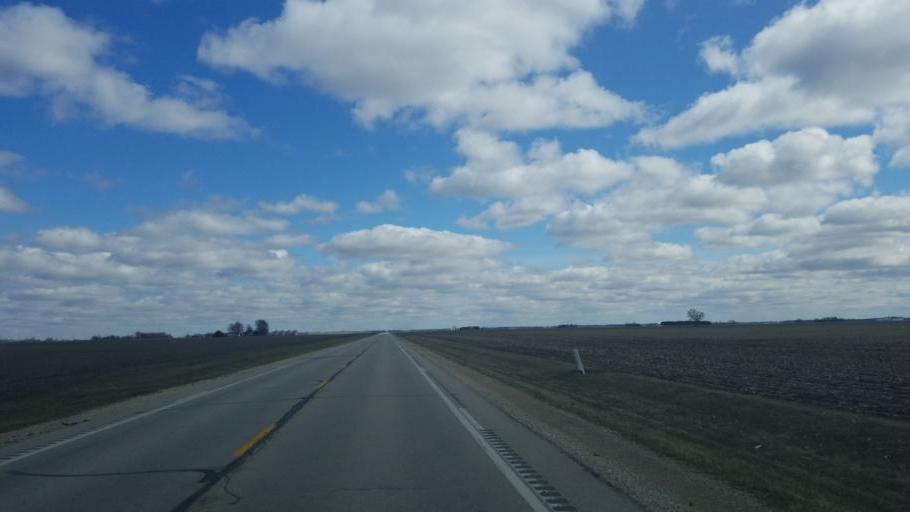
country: US
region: Illinois
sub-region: Douglas County
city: Villa Grove
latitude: 39.7919
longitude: -88.1335
